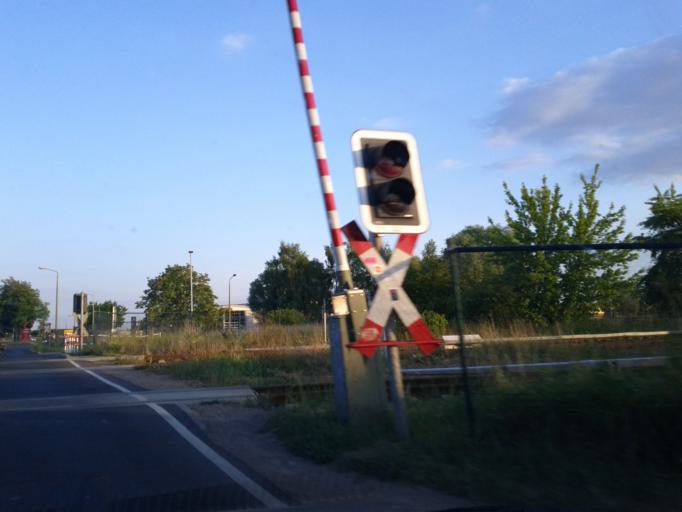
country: DE
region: Brandenburg
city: Hoppegarten
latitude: 52.5159
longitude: 13.6496
